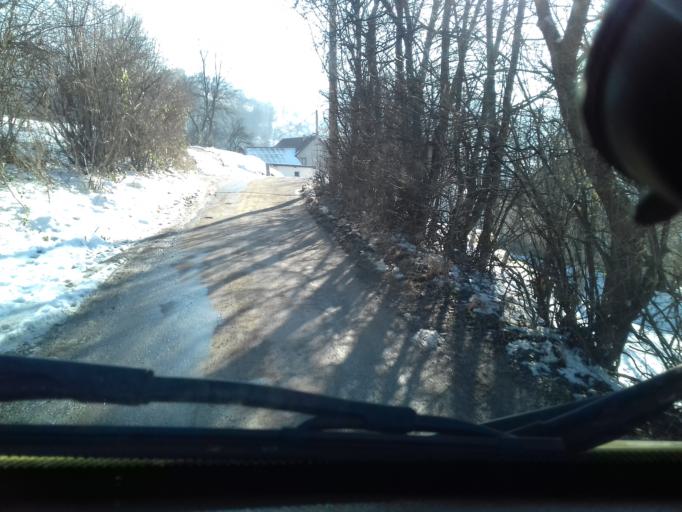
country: BA
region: Federation of Bosnia and Herzegovina
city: Zenica
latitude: 44.1844
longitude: 17.8868
